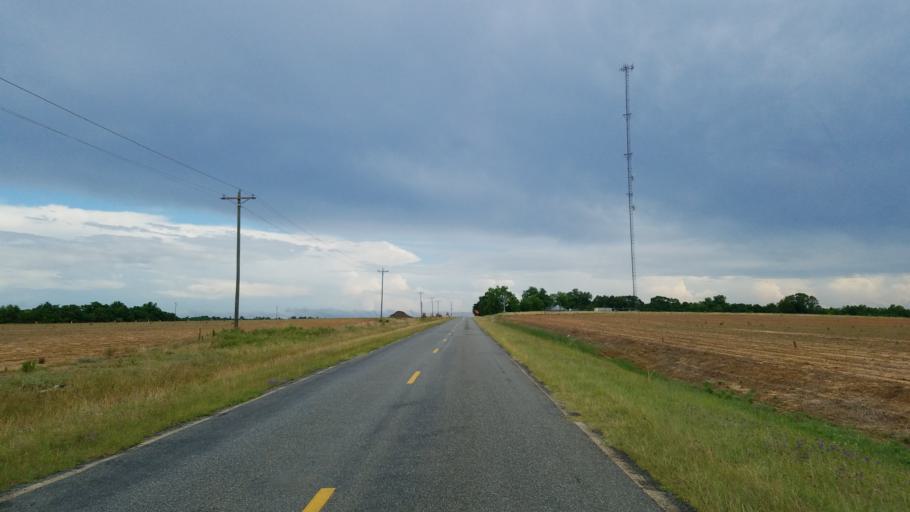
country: US
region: Georgia
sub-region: Dooly County
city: Vienna
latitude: 32.1574
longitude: -83.7981
